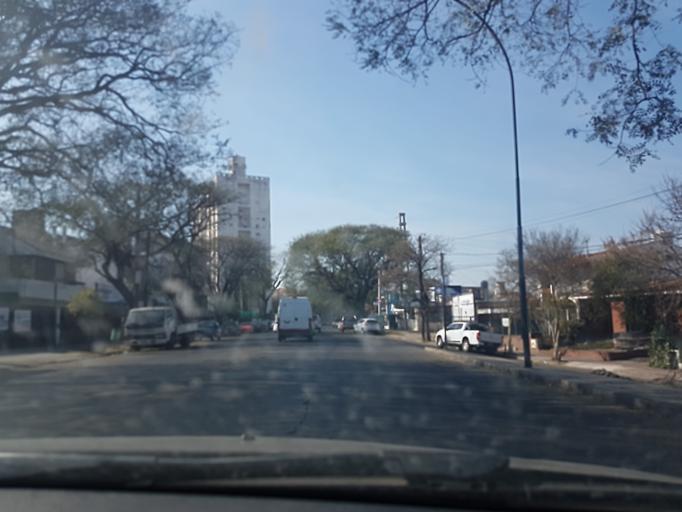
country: AR
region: Cordoba
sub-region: Departamento de Capital
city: Cordoba
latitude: -31.3862
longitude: -64.2055
